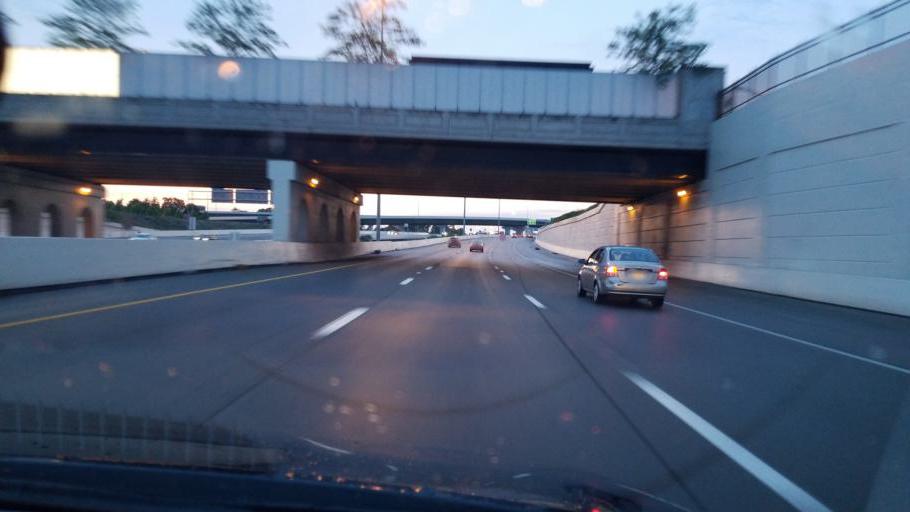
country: US
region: Ohio
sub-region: Franklin County
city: Columbus
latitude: 39.9681
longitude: -82.9835
